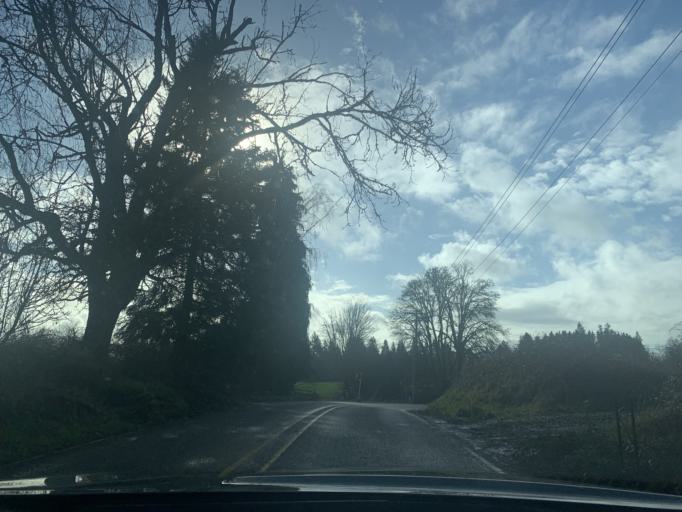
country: US
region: Oregon
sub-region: Washington County
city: Sherwood
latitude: 45.3936
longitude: -122.8436
